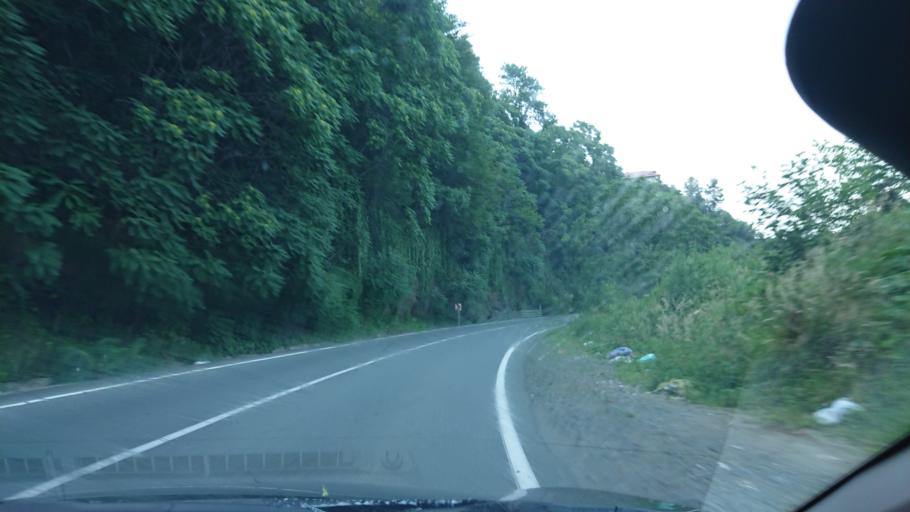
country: TR
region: Rize
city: Cayeli
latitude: 41.0757
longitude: 40.7111
